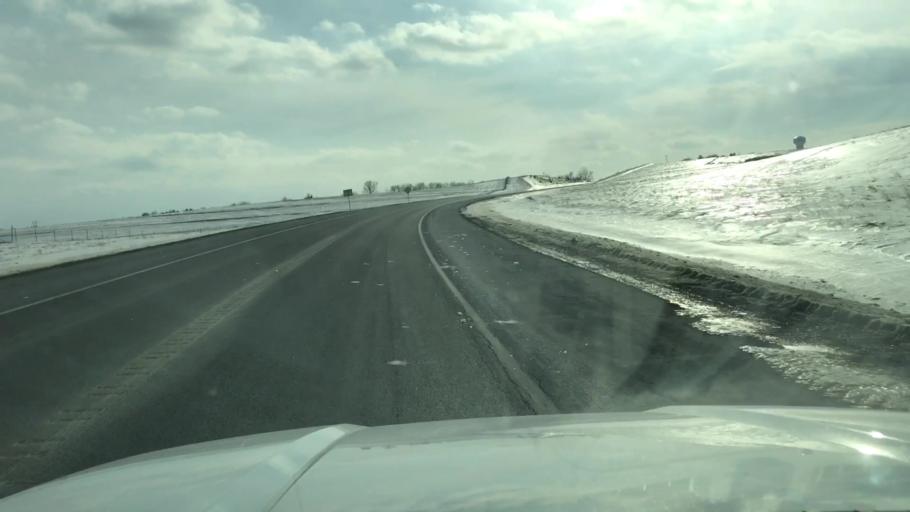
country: US
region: Missouri
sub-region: Nodaway County
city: Maryville
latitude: 40.3342
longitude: -94.8545
